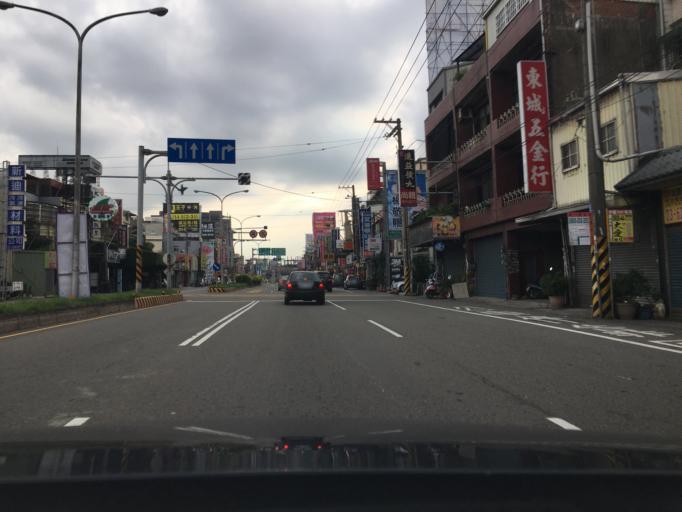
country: TW
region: Taiwan
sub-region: Hsinchu
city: Zhubei
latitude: 24.8300
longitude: 121.0010
